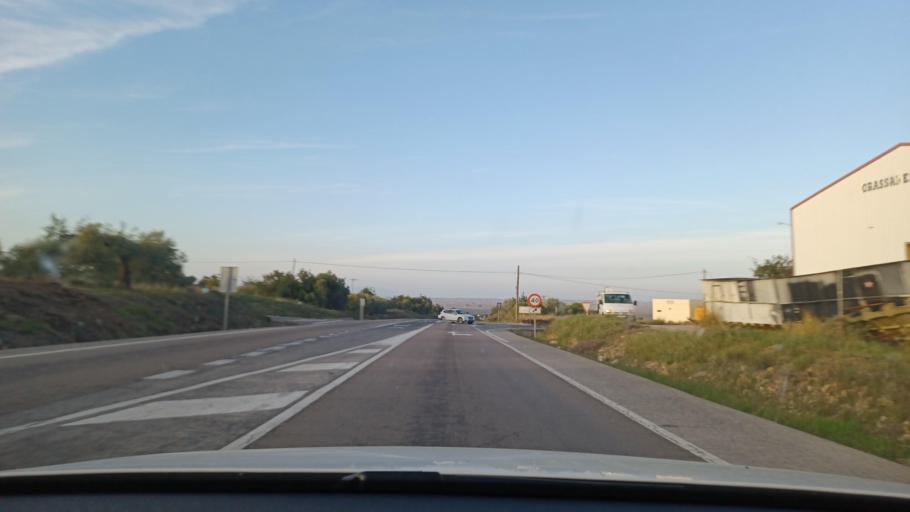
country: ES
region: Catalonia
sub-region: Provincia de Tarragona
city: Sant Carles de la Rapita
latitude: 40.6299
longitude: 0.5817
